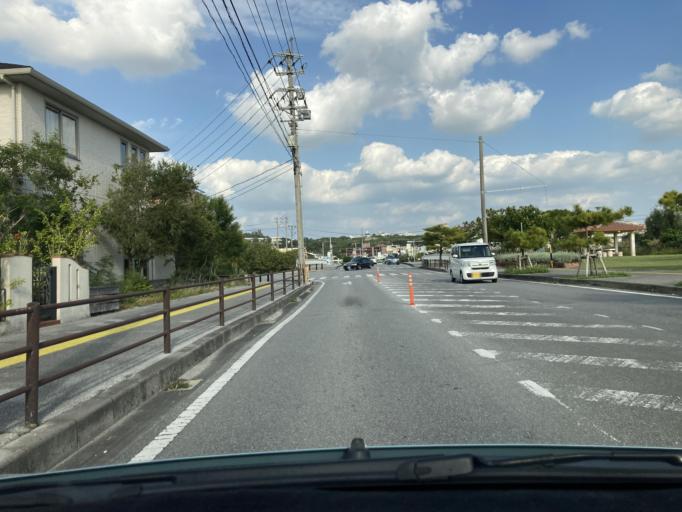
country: JP
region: Okinawa
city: Itoman
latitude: 26.1537
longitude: 127.6667
